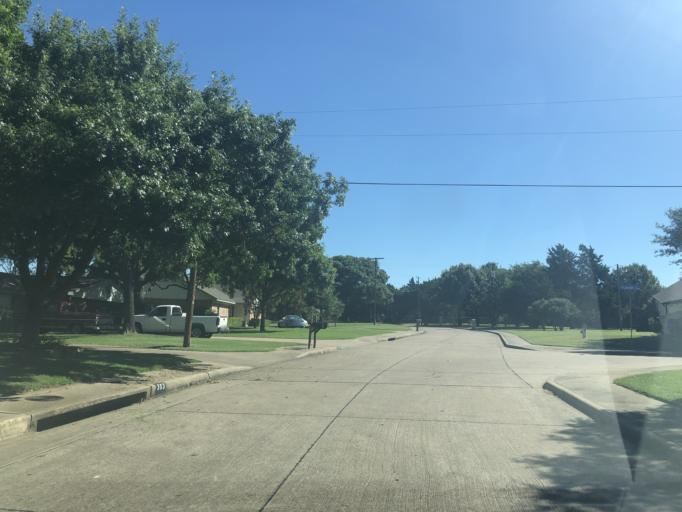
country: US
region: Texas
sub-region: Dallas County
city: Duncanville
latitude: 32.6483
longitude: -96.9389
